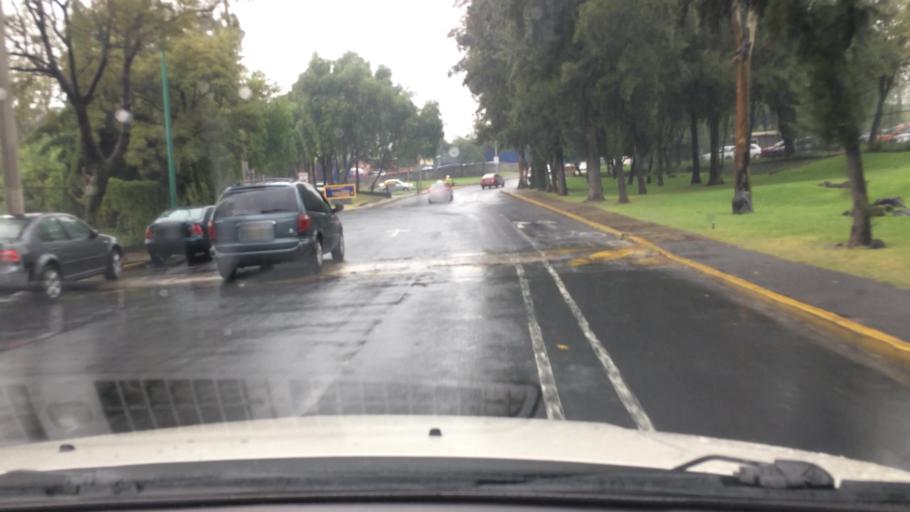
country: MX
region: Mexico City
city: Magdalena Contreras
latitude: 19.3347
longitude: -99.1939
